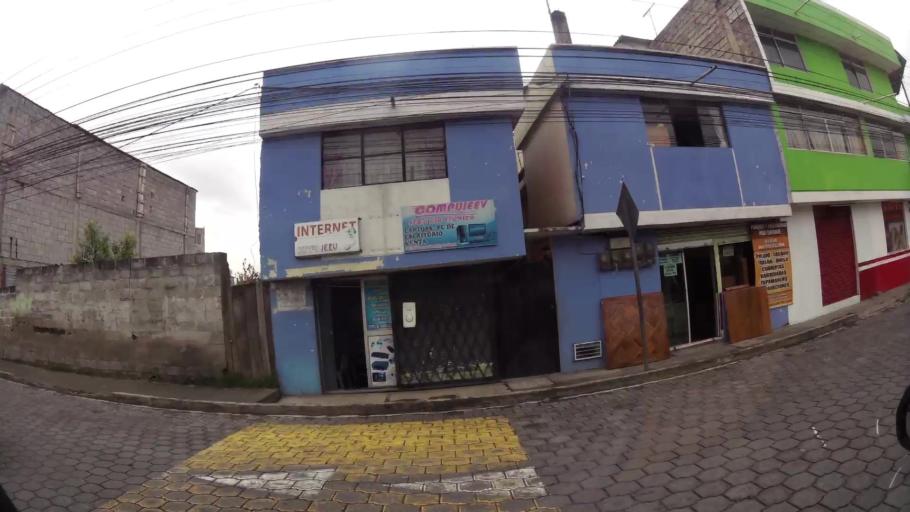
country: EC
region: Pichincha
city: Sangolqui
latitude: -0.3211
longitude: -78.4604
